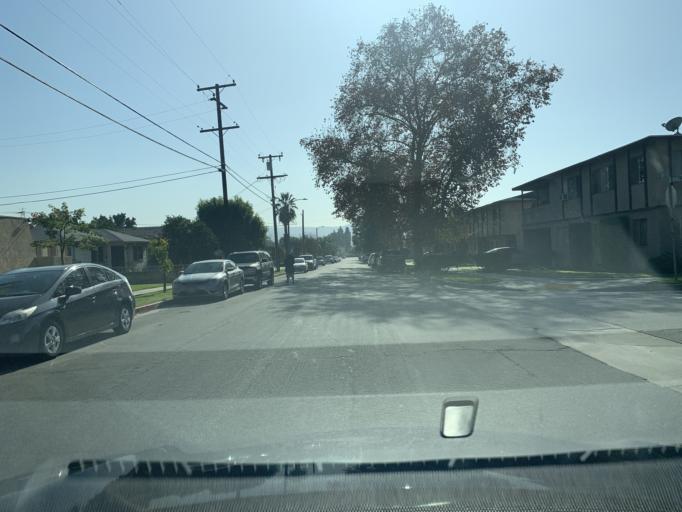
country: US
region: California
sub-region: Los Angeles County
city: Covina
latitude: 34.0820
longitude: -117.8836
